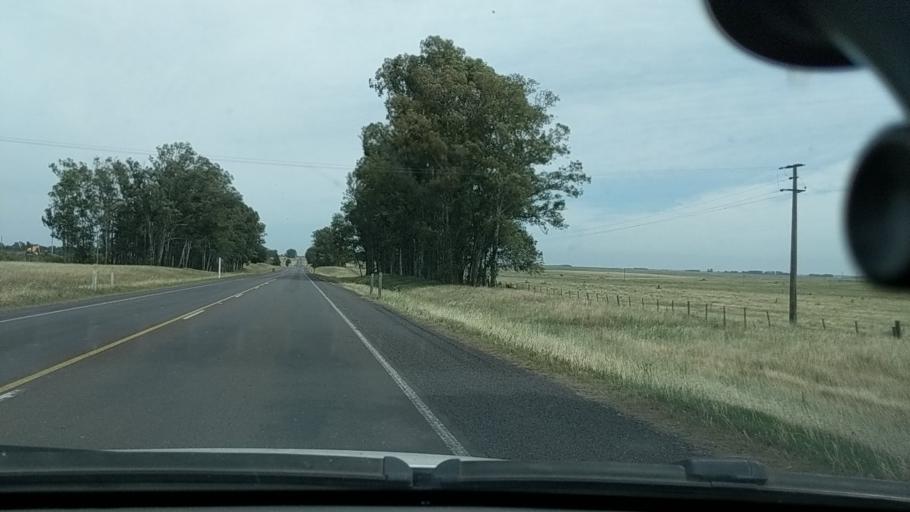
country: UY
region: Durazno
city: Durazno
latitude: -33.4742
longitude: -56.4509
